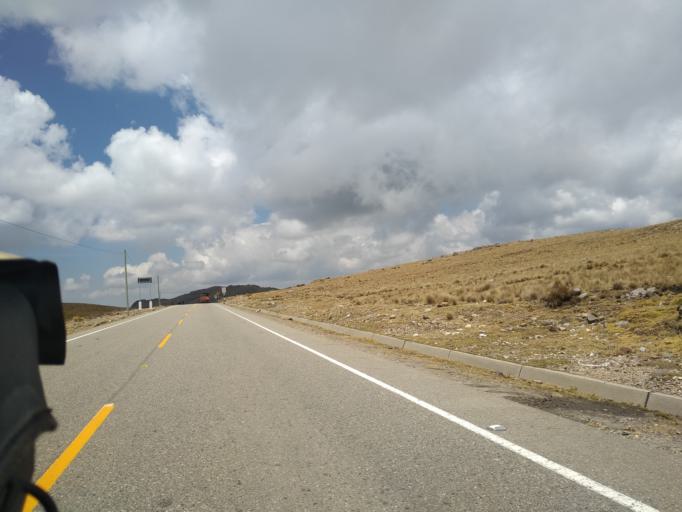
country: PE
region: La Libertad
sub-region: Provincia de Santiago de Chuco
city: Quiruvilca
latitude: -7.9670
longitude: -78.1991
